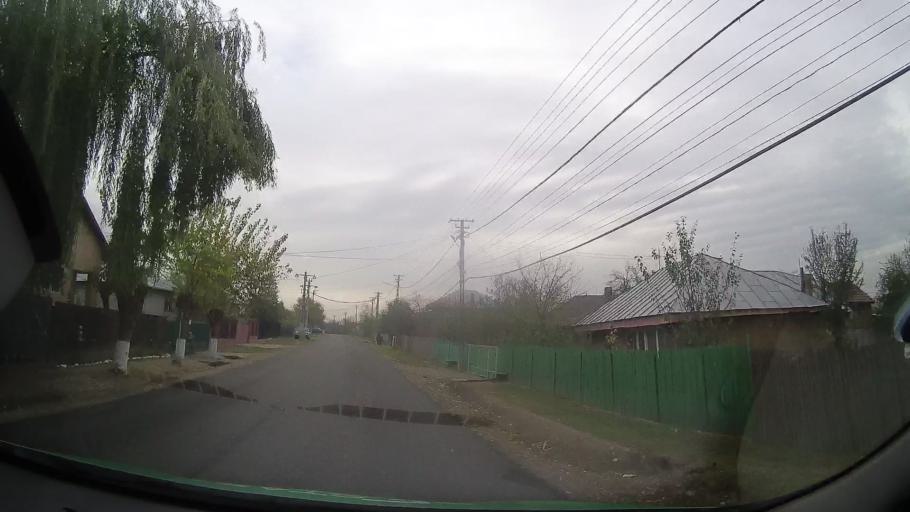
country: RO
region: Prahova
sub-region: Comuna Valea Calugareasca
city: Pantazi
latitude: 44.9329
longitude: 26.1410
